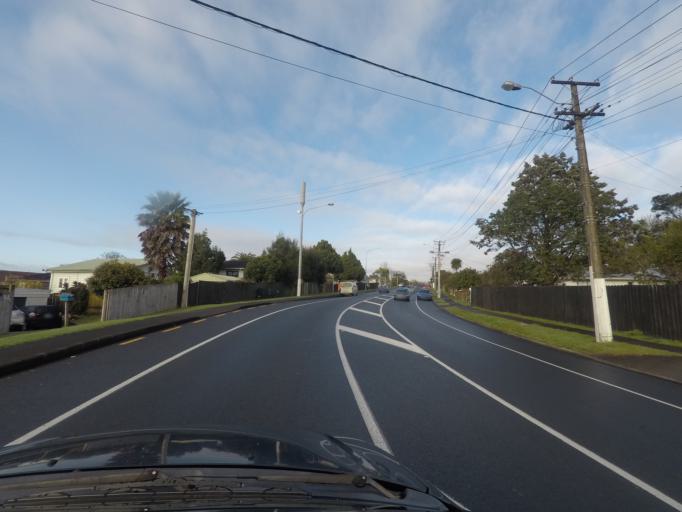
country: NZ
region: Auckland
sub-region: Auckland
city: Waitakere
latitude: -36.8965
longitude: 174.6193
